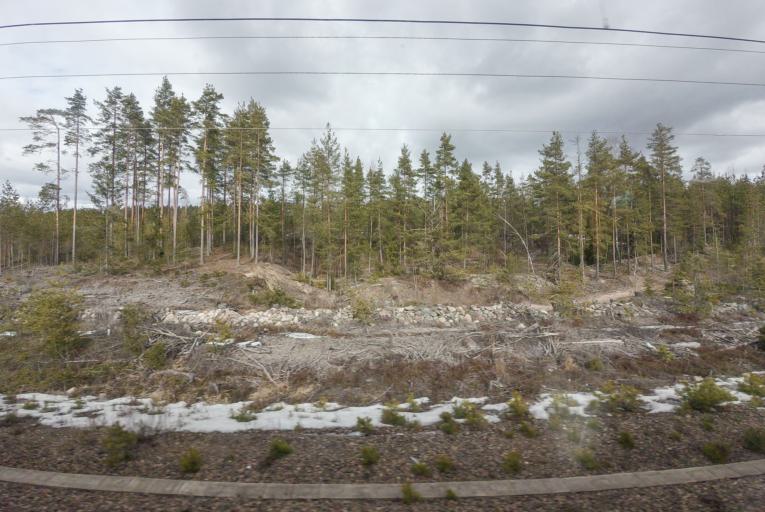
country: FI
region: Kymenlaakso
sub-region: Kouvola
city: Iitti
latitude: 60.9209
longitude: 26.1532
